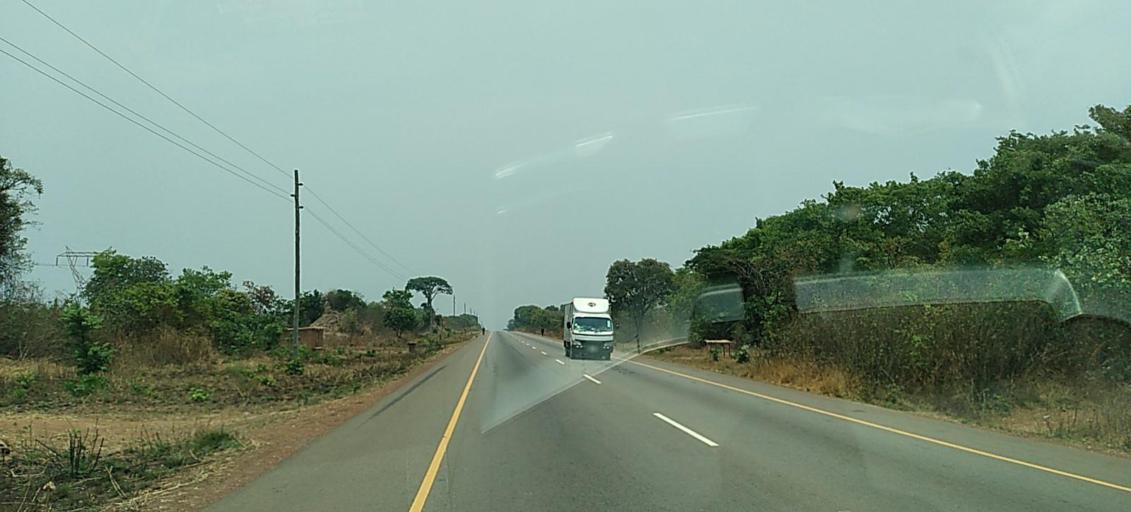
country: ZM
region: Copperbelt
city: Chililabombwe
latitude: -12.4976
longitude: 27.5358
